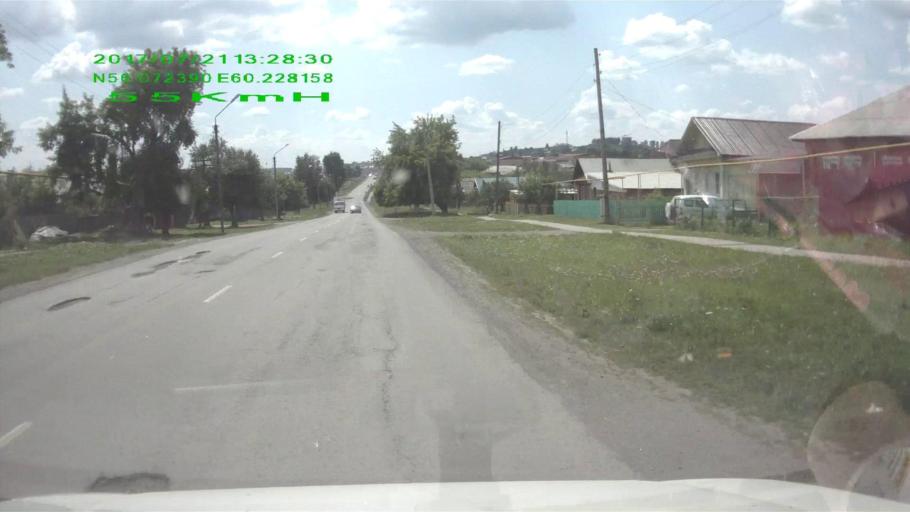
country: RU
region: Chelyabinsk
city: Verkhniy Ufaley
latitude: 56.0716
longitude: 60.2274
